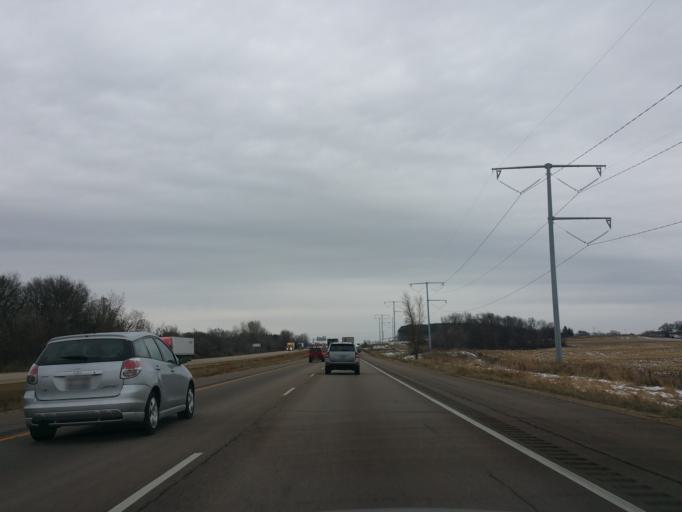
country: US
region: Wisconsin
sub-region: Dane County
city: McFarland
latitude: 43.0369
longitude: -89.2703
